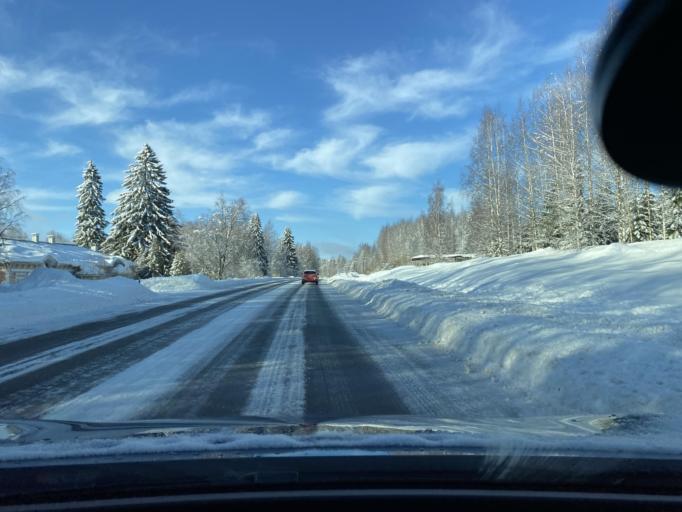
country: FI
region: Southern Savonia
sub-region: Mikkeli
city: Kangasniemi
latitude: 62.0131
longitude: 26.6252
